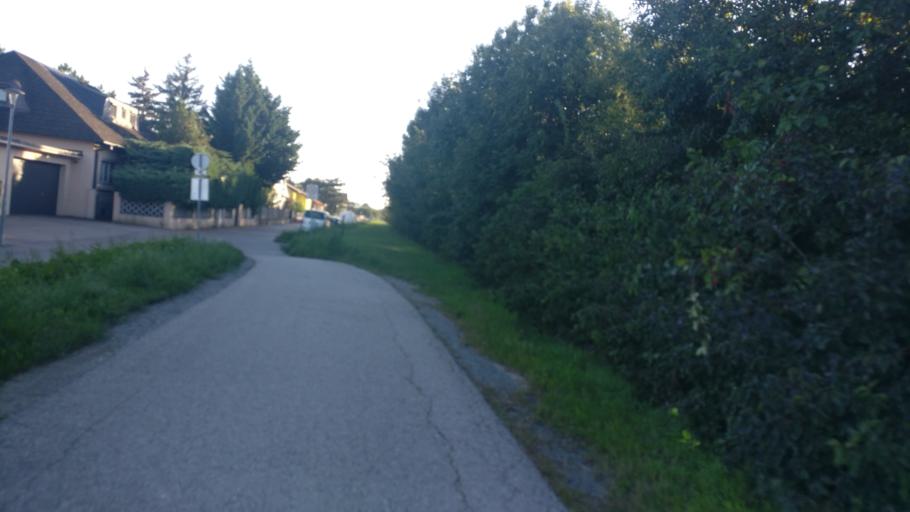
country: AT
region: Lower Austria
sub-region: Politischer Bezirk Wien-Umgebung
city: Himberg
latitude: 48.0910
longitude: 16.4373
